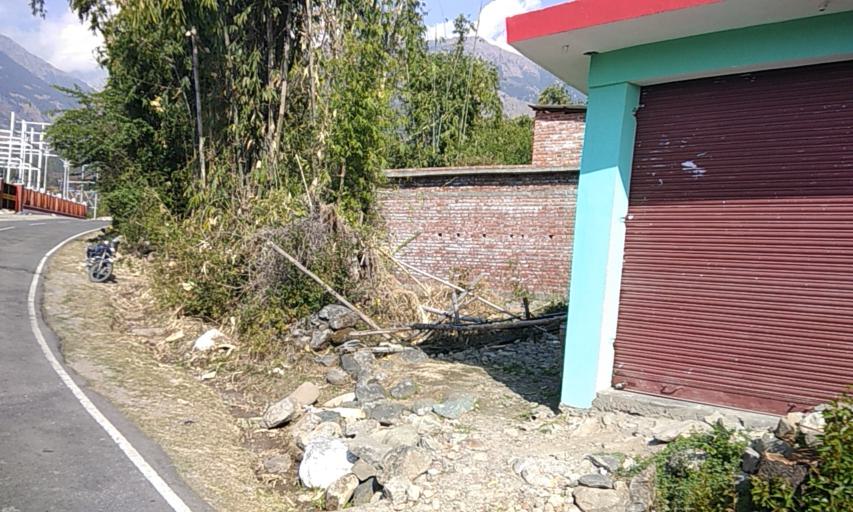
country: IN
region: Himachal Pradesh
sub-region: Kangra
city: Dharmsala
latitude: 32.1590
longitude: 76.4062
